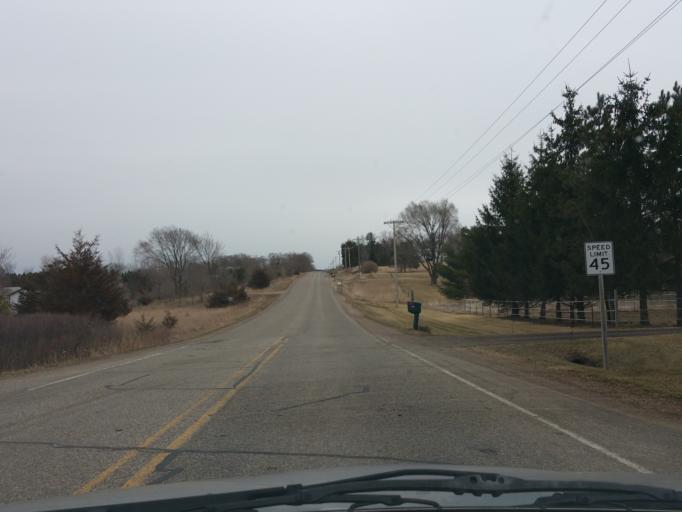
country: US
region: Wisconsin
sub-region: Saint Croix County
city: Roberts
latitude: 45.0033
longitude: -92.6450
